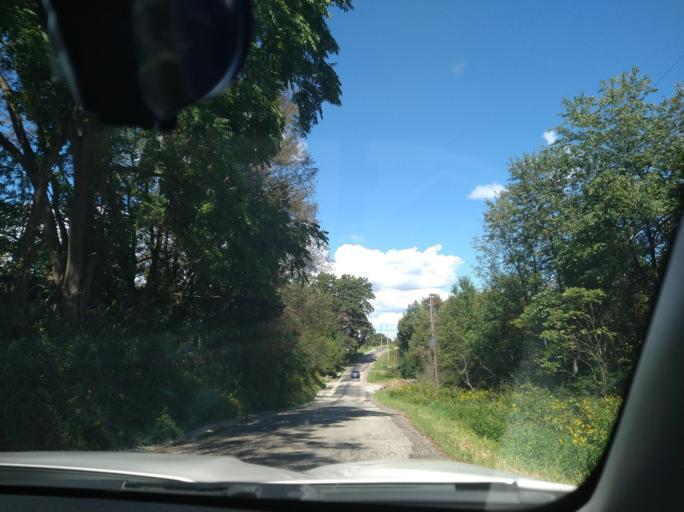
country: US
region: Pennsylvania
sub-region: Fayette County
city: Bear Rocks
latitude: 40.0942
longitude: -79.3652
